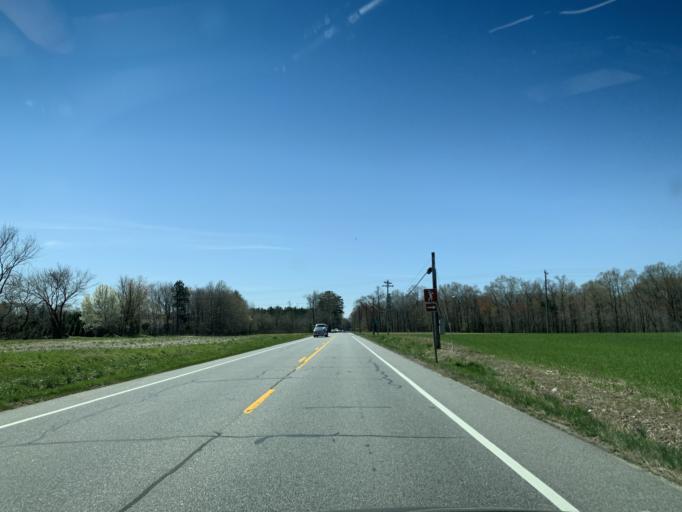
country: US
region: Maryland
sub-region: Talbot County
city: Easton
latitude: 38.8241
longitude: -76.0392
